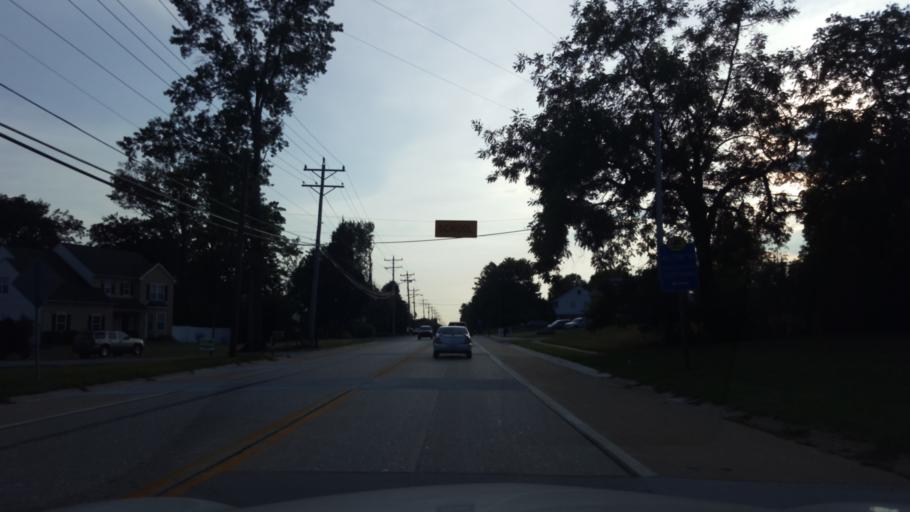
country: US
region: Delaware
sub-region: New Castle County
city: Pike Creek Valley
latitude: 39.7359
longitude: -75.6538
